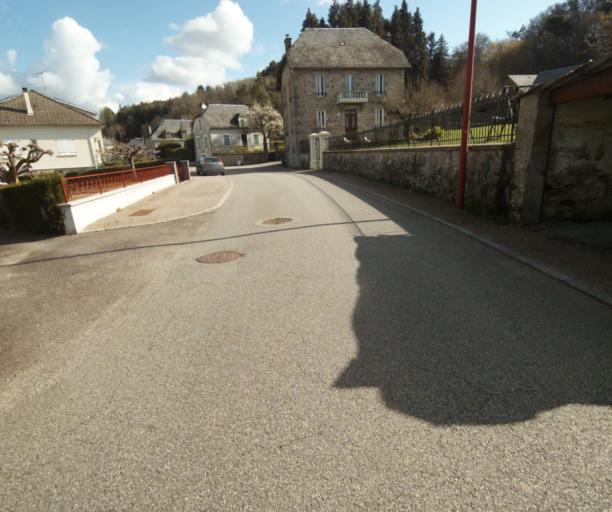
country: FR
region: Limousin
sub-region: Departement de la Correze
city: Laguenne
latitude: 45.2306
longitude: 1.8974
